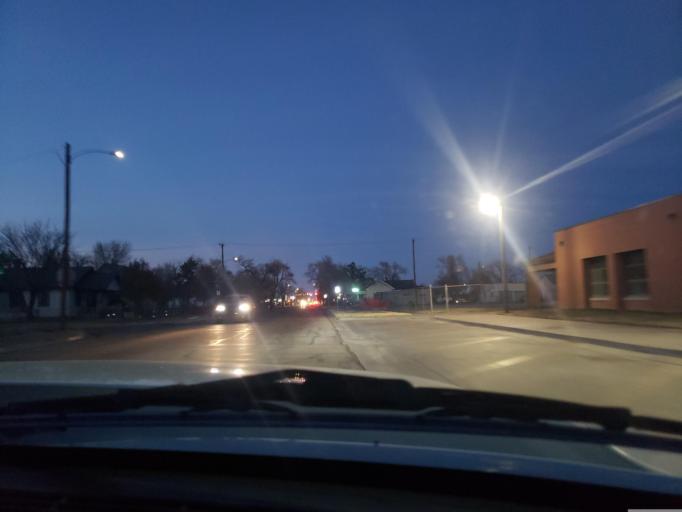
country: US
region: Kansas
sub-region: Finney County
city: Garden City
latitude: 37.9721
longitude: -100.8833
